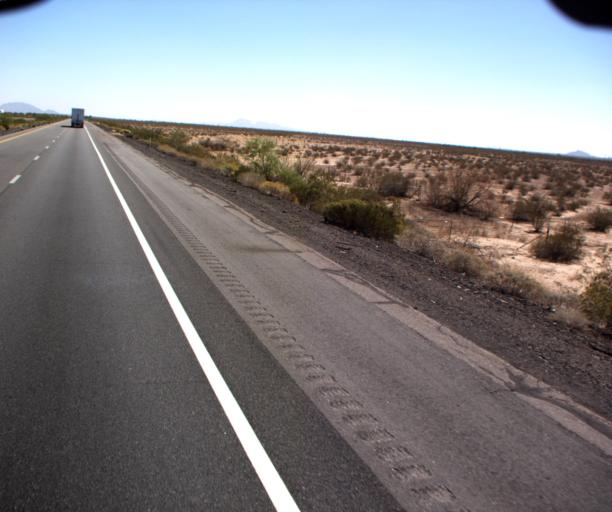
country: US
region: Arizona
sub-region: La Paz County
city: Salome
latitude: 33.5733
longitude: -113.3837
